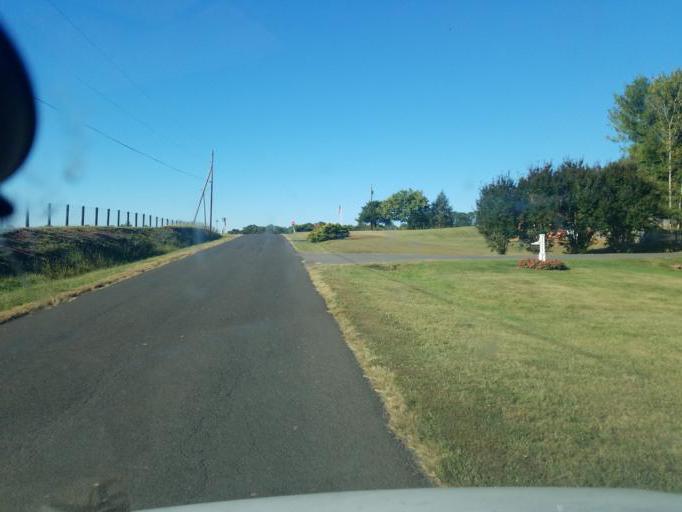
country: US
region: Virginia
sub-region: Fauquier County
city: Bealeton
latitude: 38.5515
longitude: -77.8151
